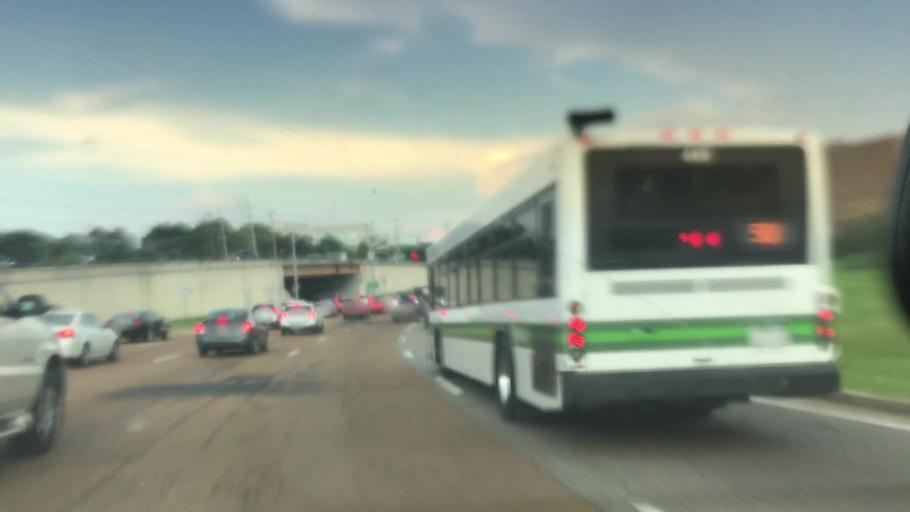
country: US
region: Tennessee
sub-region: Shelby County
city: Germantown
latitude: 35.1025
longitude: -89.8650
